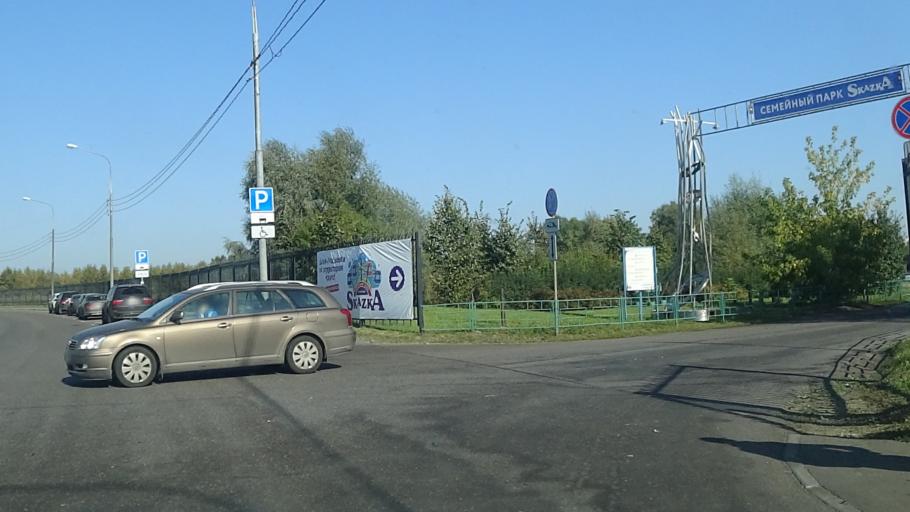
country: RU
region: Moscow
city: Shchukino
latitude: 55.7692
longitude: 37.4283
